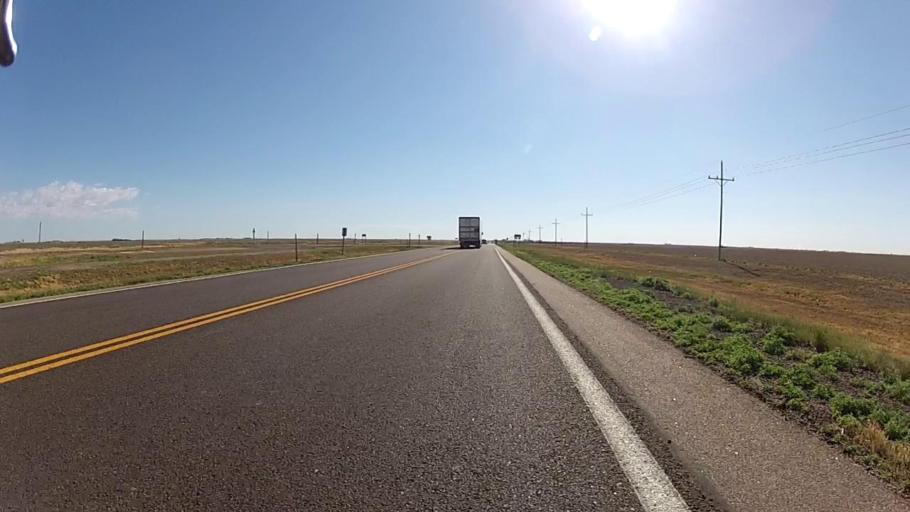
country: US
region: Kansas
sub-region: Haskell County
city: Sublette
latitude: 37.5616
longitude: -100.5656
